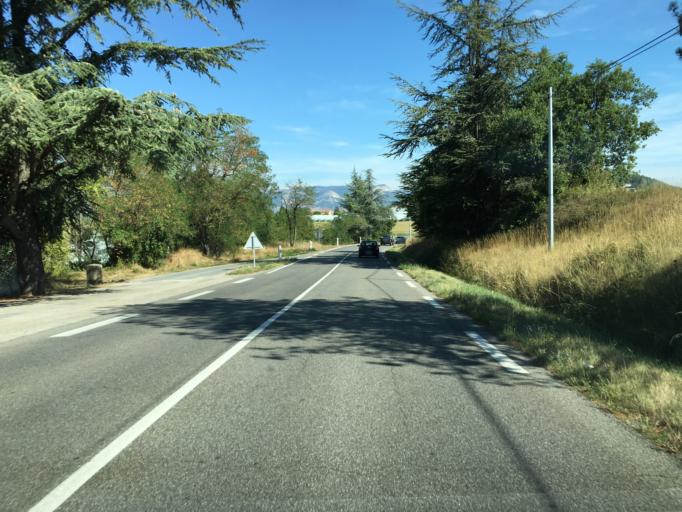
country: FR
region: Provence-Alpes-Cote d'Azur
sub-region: Departement des Hautes-Alpes
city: Laragne-Monteglin
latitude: 44.2724
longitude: 5.8536
